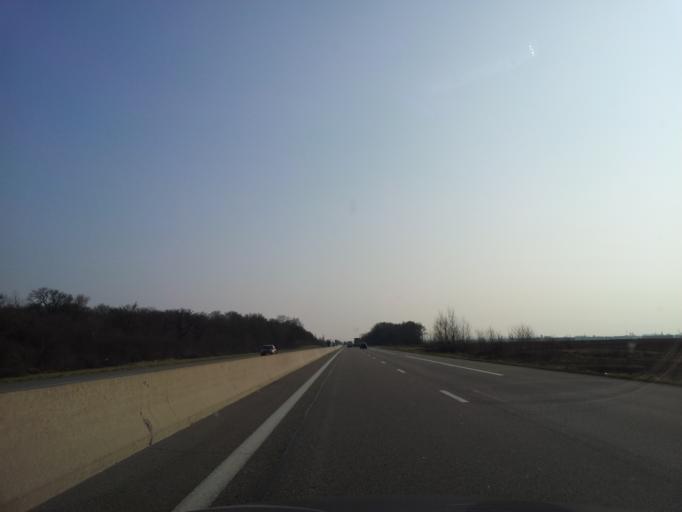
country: FR
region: Alsace
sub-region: Departement du Haut-Rhin
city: Battenheim
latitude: 47.8453
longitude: 7.3946
